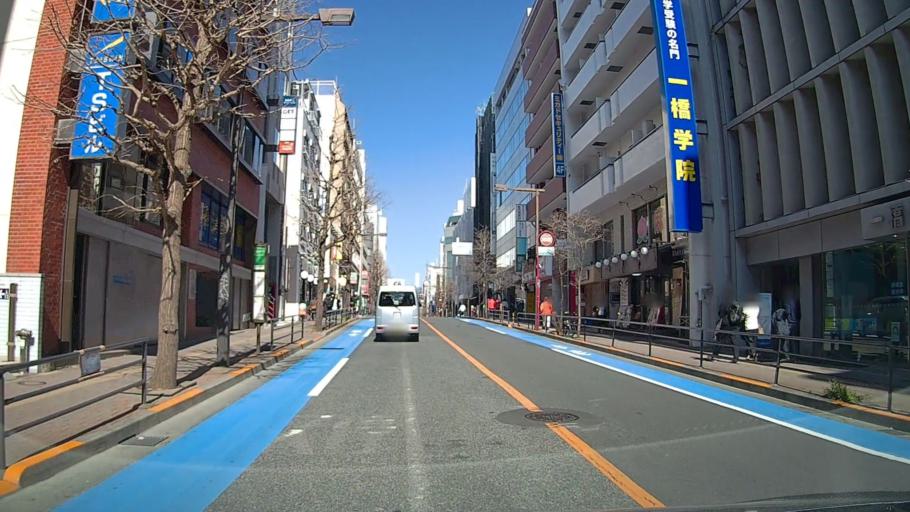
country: JP
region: Tokyo
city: Tokyo
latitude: 35.7104
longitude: 139.7038
